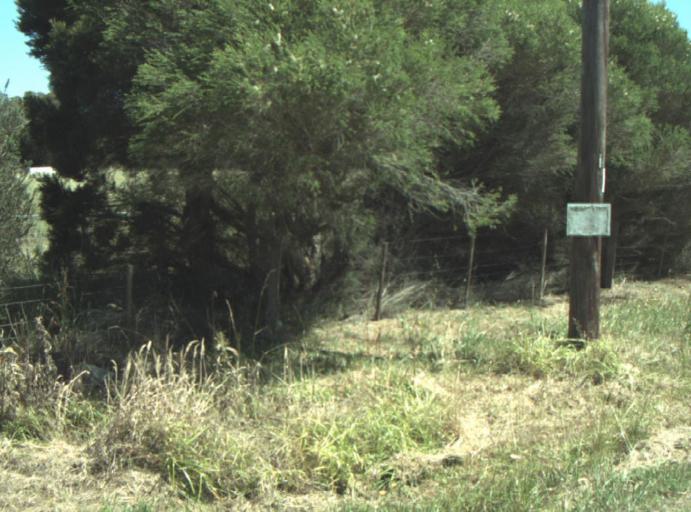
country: AU
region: Victoria
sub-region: Greater Geelong
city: Breakwater
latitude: -38.2527
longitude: 144.3504
